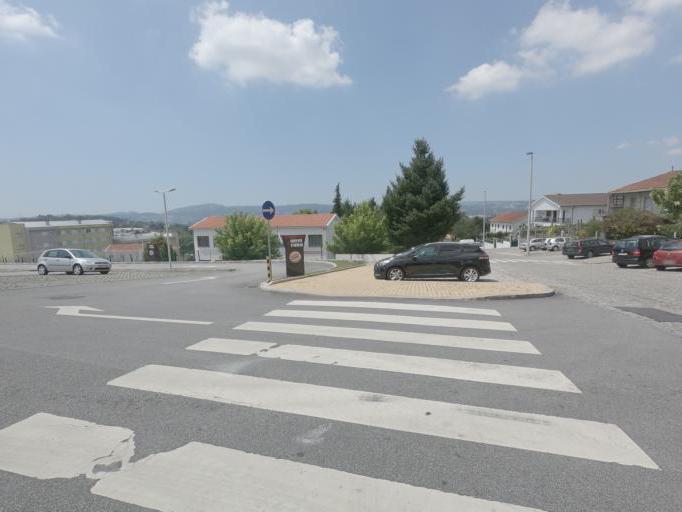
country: PT
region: Porto
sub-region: Penafiel
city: Penafiel
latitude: 41.1960
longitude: -8.2962
